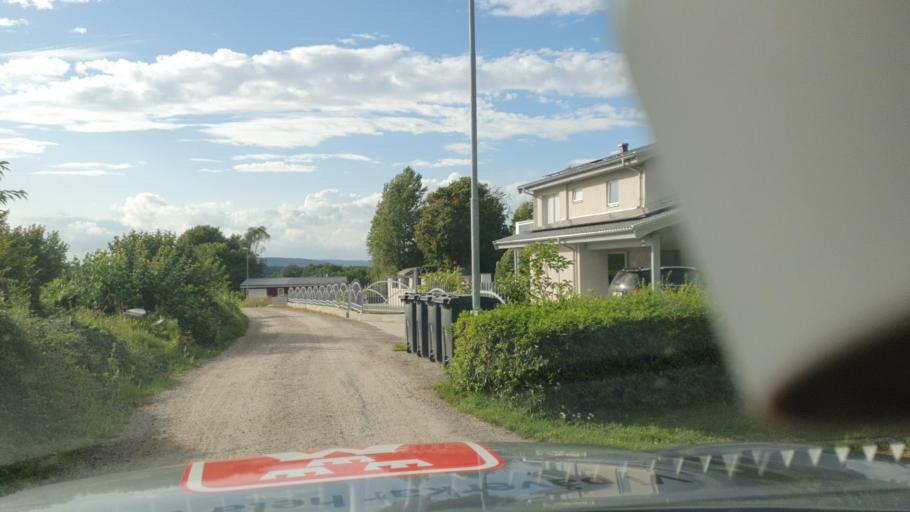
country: SE
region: Skane
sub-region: Bromolla Kommun
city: Bromoella
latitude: 56.0946
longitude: 14.4936
